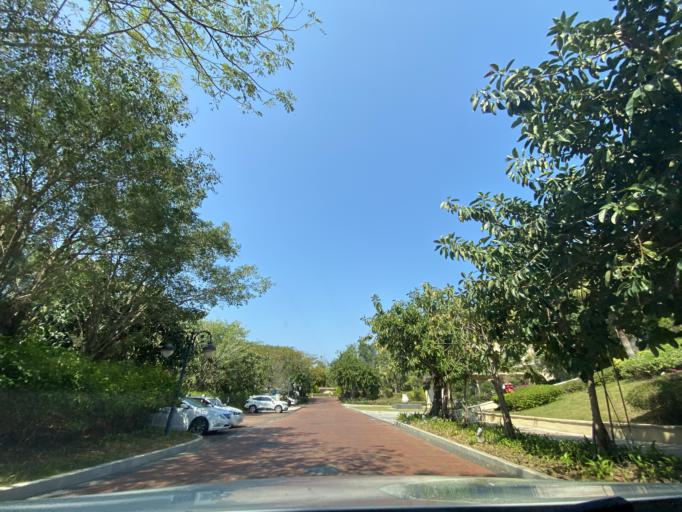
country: CN
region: Hainan
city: Haitangwan
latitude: 18.3501
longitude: 109.7359
